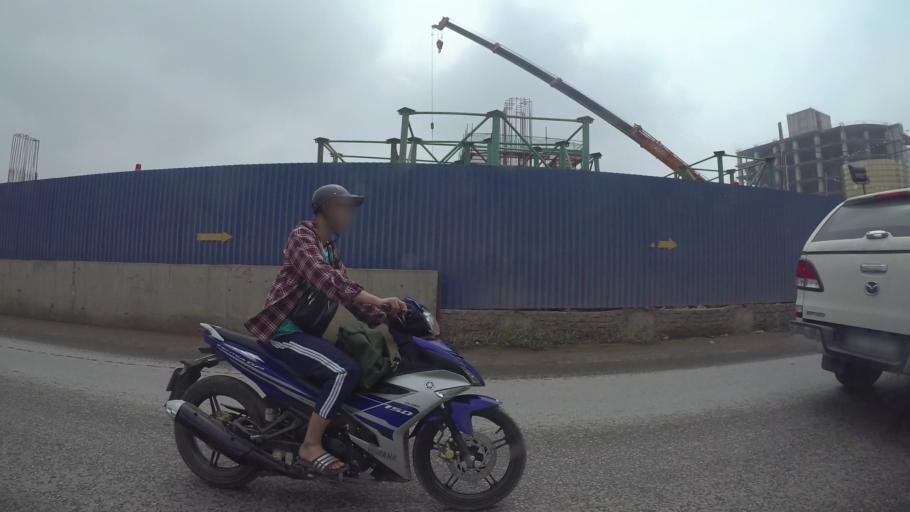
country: VN
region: Ha Noi
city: Cau Dien
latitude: 21.0546
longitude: 105.7818
